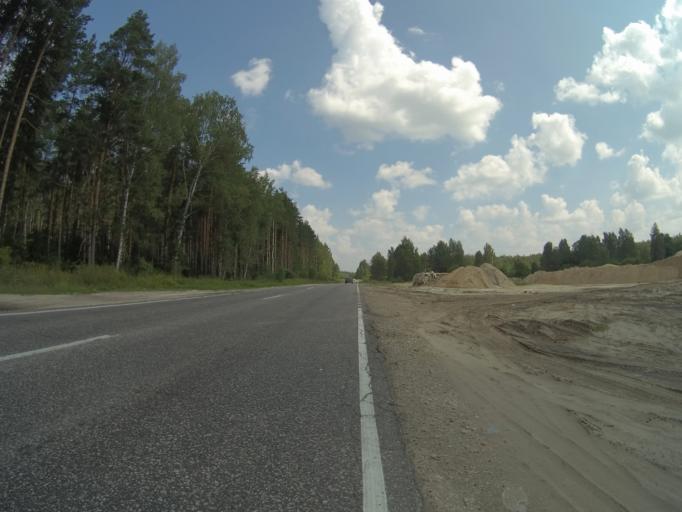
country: RU
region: Vladimir
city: Gus'-Khrustal'nyy
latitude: 55.6368
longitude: 40.7301
